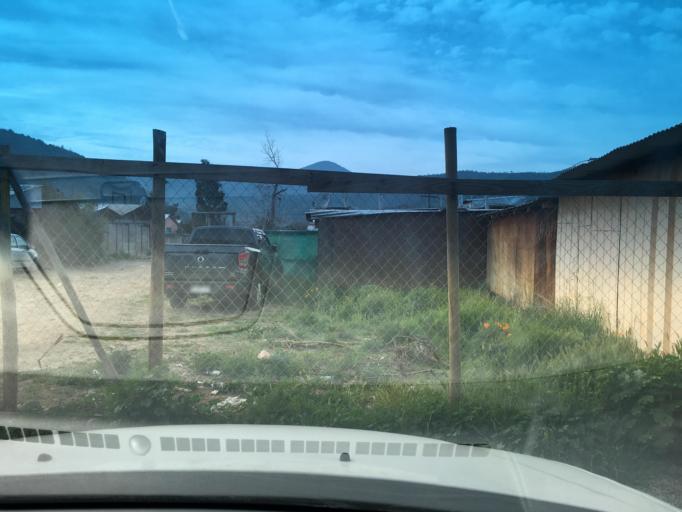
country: CL
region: Santiago Metropolitan
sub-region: Provincia de Chacabuco
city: Lampa
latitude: -33.0756
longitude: -70.9286
